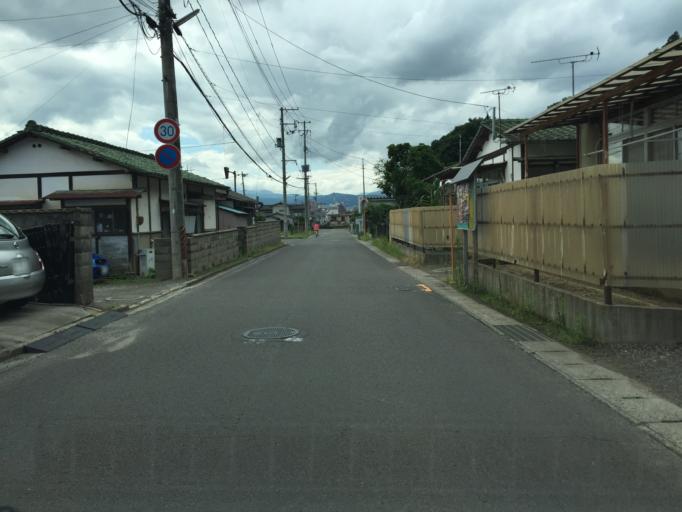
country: JP
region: Fukushima
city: Fukushima-shi
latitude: 37.7479
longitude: 140.4886
